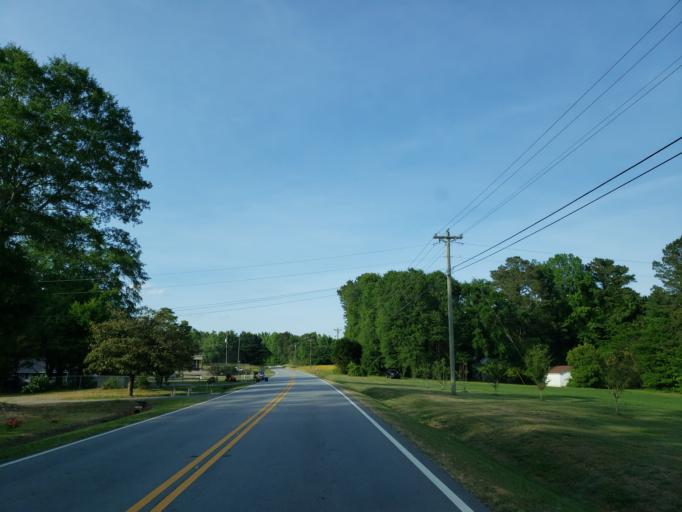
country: US
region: Georgia
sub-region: Carroll County
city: Bowdon
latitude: 33.5112
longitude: -85.2654
